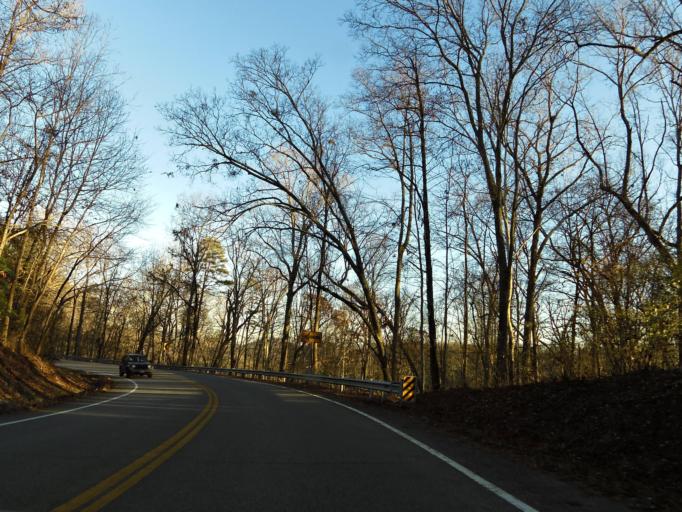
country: US
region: Tennessee
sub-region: Anderson County
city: Norris
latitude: 36.2228
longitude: -84.0984
